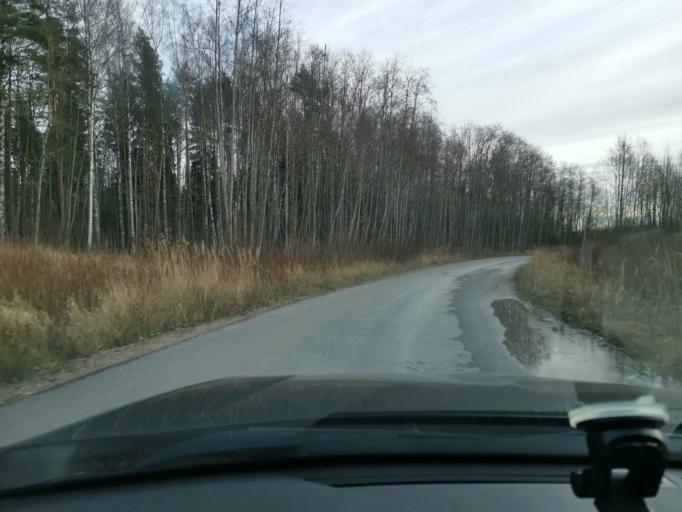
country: EE
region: Ida-Virumaa
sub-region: Sillamaee linn
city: Sillamae
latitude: 59.2629
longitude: 27.9059
